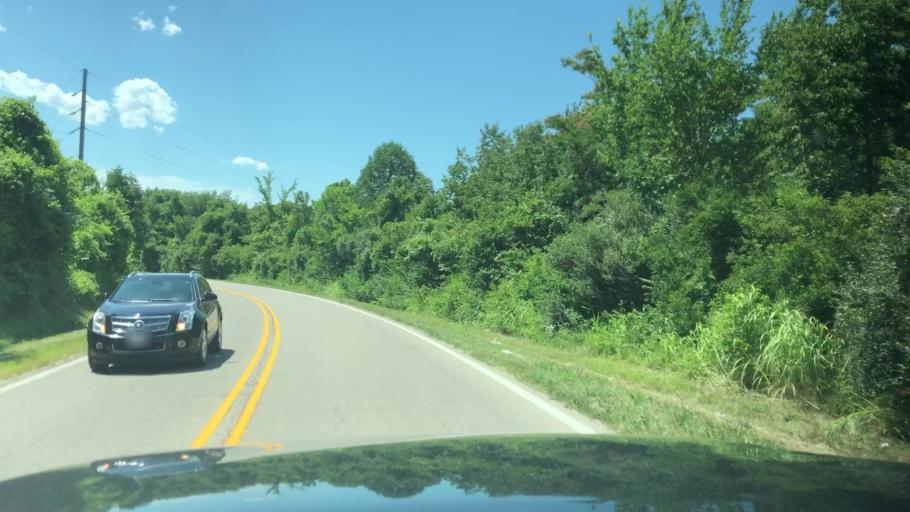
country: US
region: Illinois
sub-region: Saint Clair County
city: Centreville
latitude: 38.5542
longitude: -90.0825
